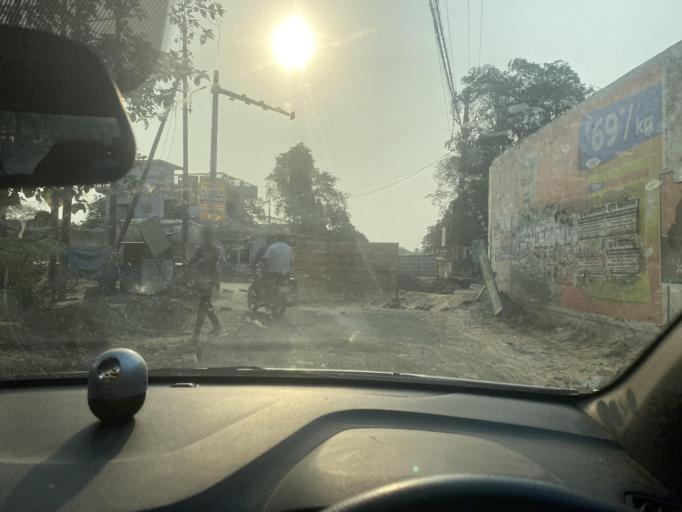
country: IN
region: Uttar Pradesh
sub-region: Faizabad
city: Ayodhya
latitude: 26.7834
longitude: 82.1907
